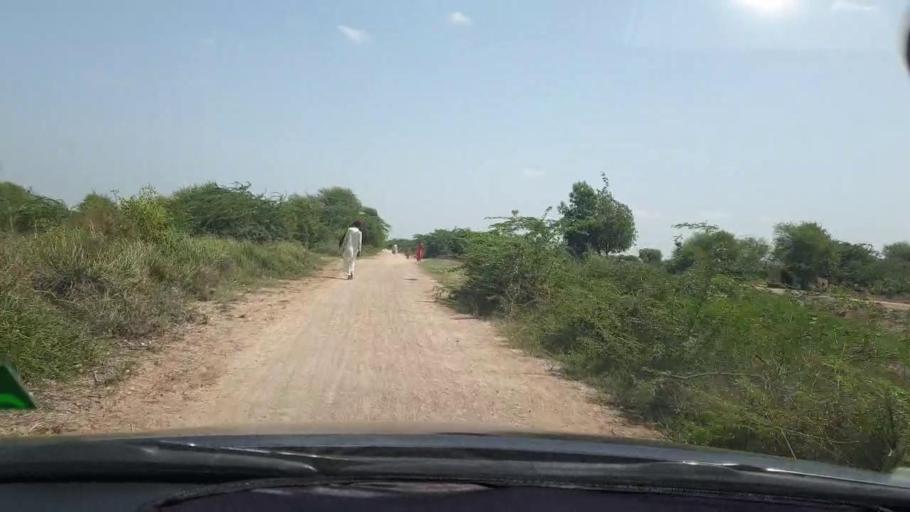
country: PK
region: Sindh
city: Tando Bago
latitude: 24.8965
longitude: 69.0830
